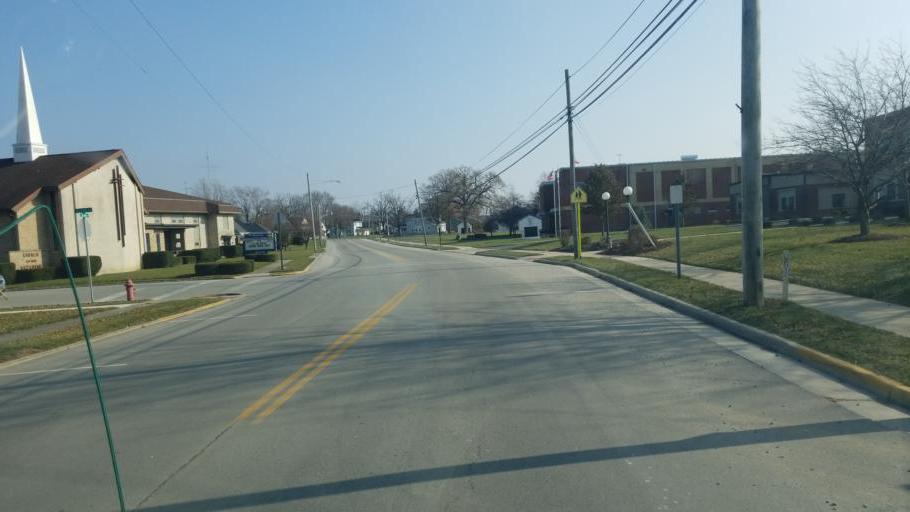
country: US
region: Ohio
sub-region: Mercer County
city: Fort Recovery
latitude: 40.4128
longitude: -84.7753
